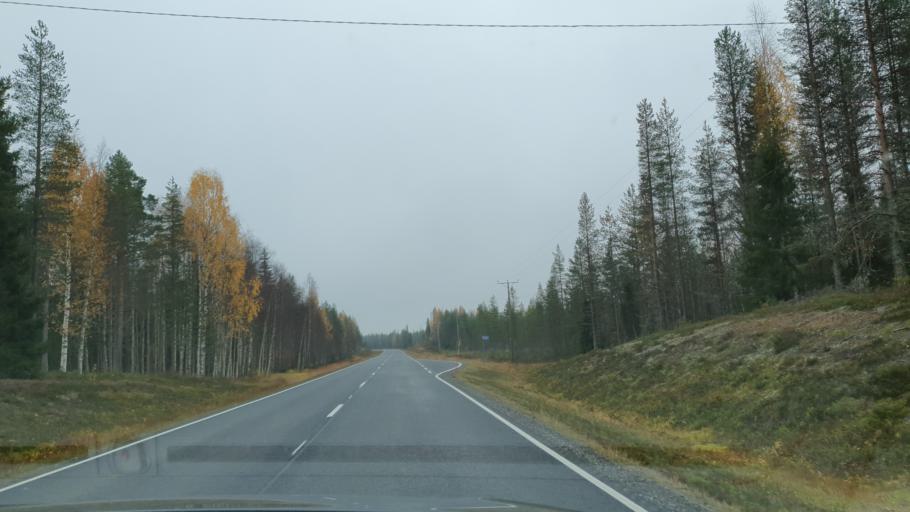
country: FI
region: Lapland
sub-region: Rovaniemi
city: Ranua
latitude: 66.1381
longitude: 26.2737
